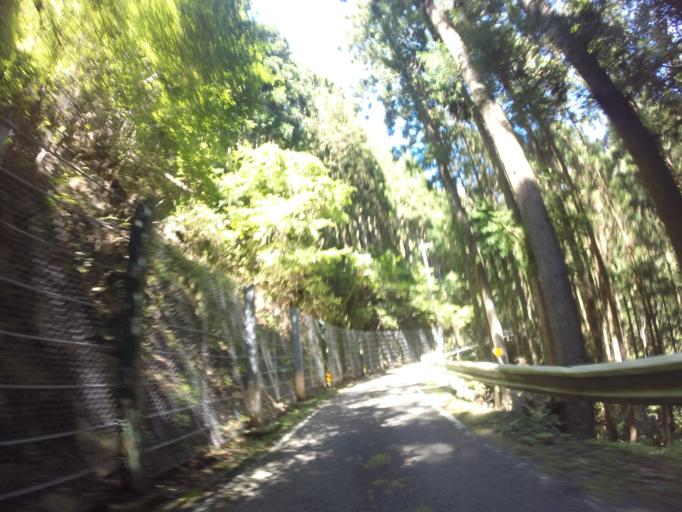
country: JP
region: Shizuoka
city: Fujieda
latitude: 34.9830
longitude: 138.1930
